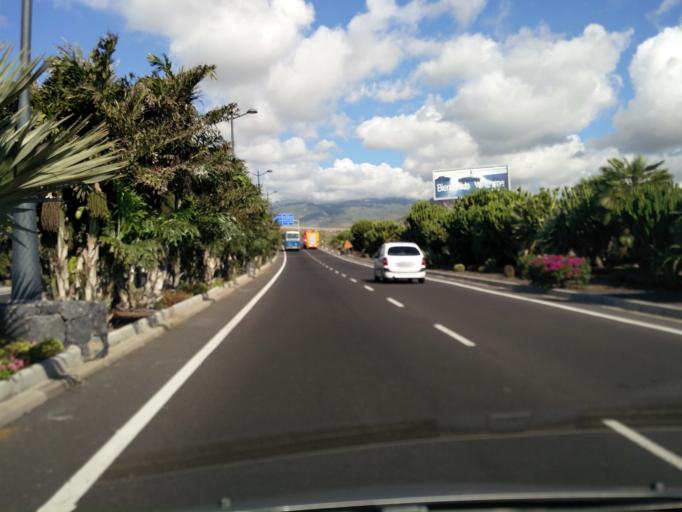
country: ES
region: Canary Islands
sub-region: Provincia de Santa Cruz de Tenerife
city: San Isidro
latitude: 28.0547
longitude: -16.5788
